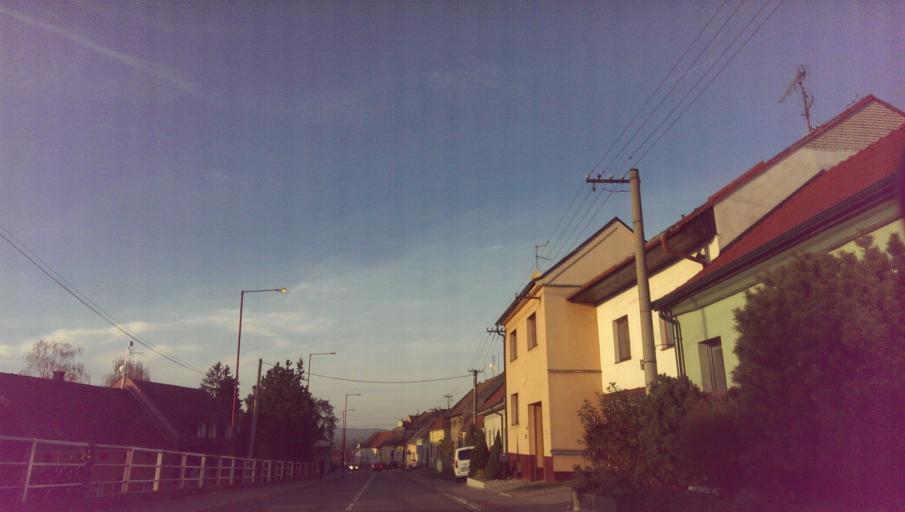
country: CZ
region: Zlin
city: Kunovice
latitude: 49.0636
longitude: 17.4815
